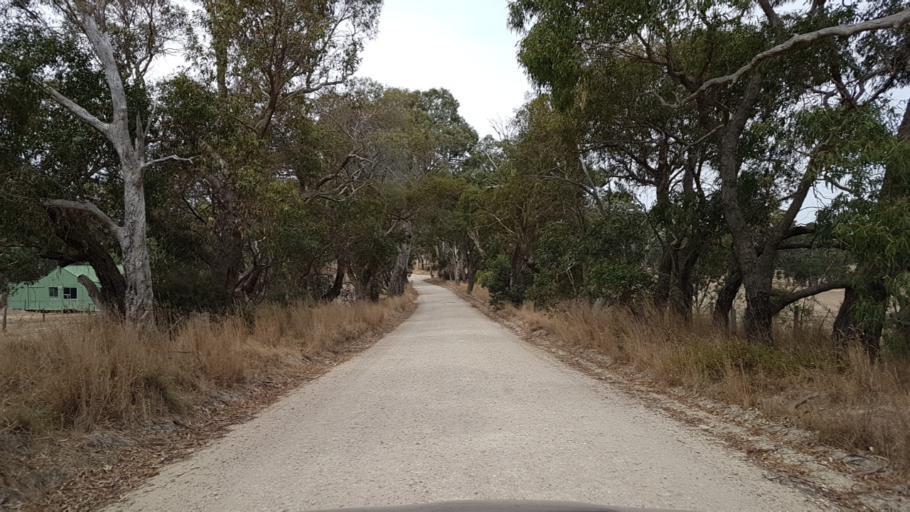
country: AU
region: South Australia
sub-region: Adelaide Hills
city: Birdwood
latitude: -34.7618
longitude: 139.0046
